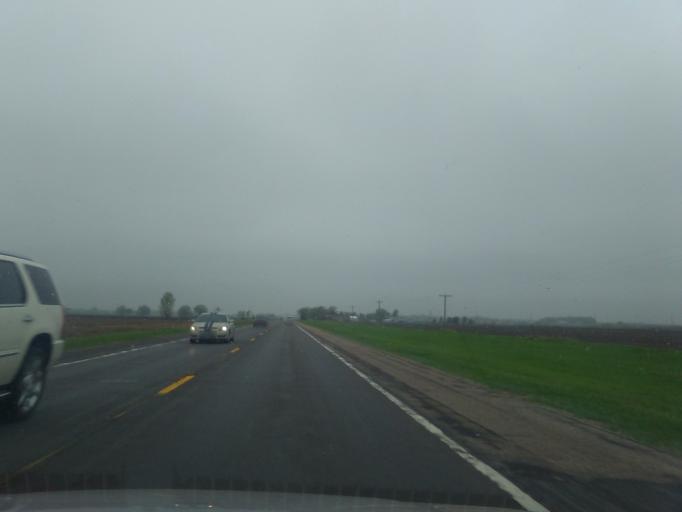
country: US
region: Nebraska
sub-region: Cuming County
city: West Point
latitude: 41.9106
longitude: -96.7802
